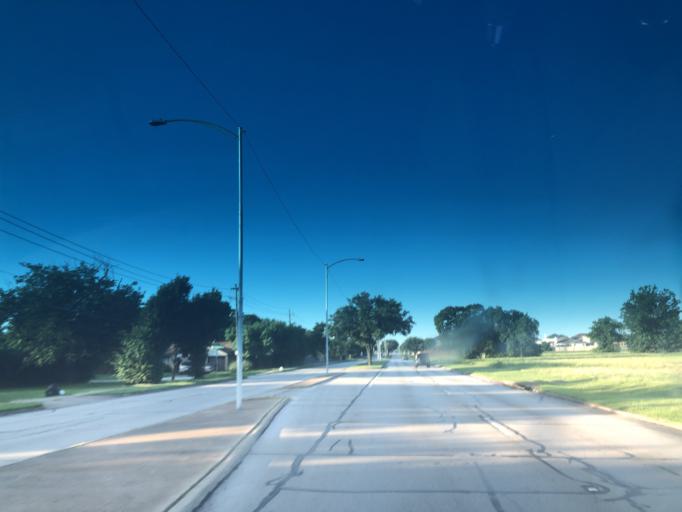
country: US
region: Texas
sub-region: Dallas County
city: Grand Prairie
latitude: 32.7040
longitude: -97.0155
